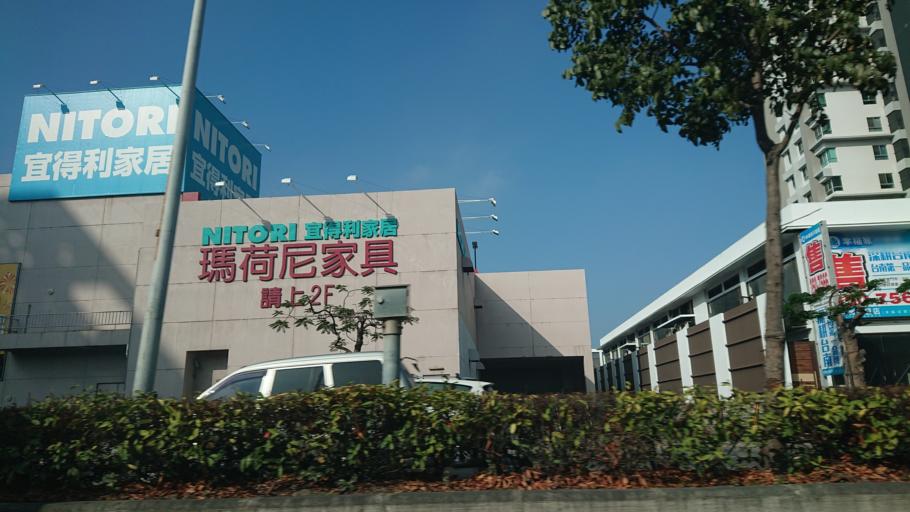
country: TW
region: Taiwan
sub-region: Tainan
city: Tainan
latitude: 23.0026
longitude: 120.1870
